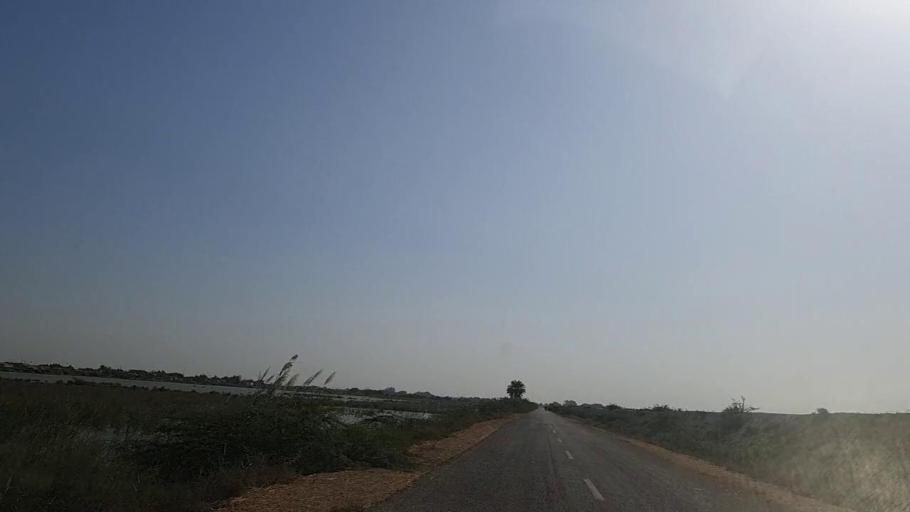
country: PK
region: Sindh
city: Jati
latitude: 24.4377
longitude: 68.2605
